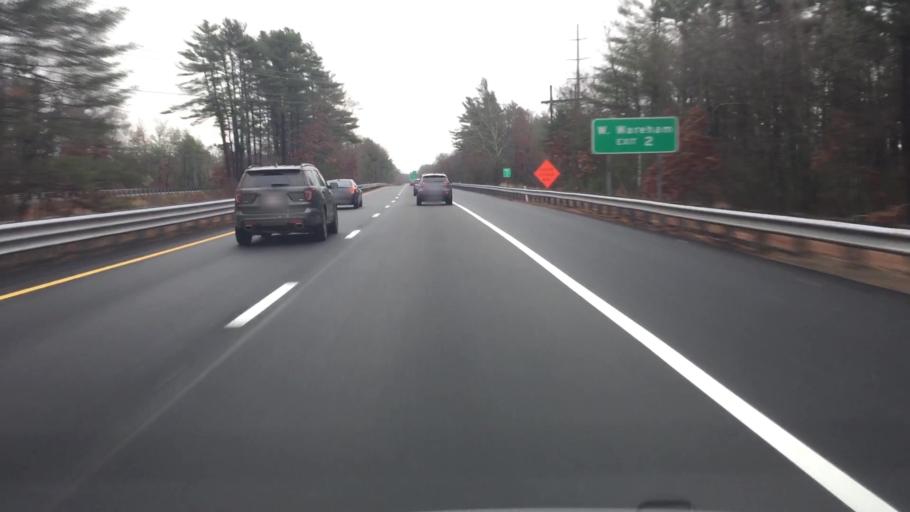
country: US
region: Massachusetts
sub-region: Plymouth County
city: West Wareham
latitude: 41.8113
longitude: -70.7905
